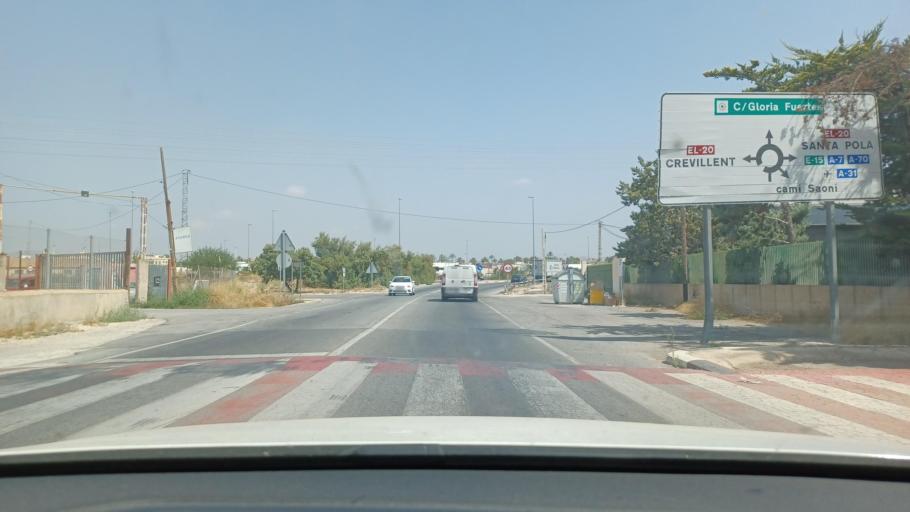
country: ES
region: Valencia
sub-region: Provincia de Alicante
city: Elche
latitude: 38.2510
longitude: -0.6918
